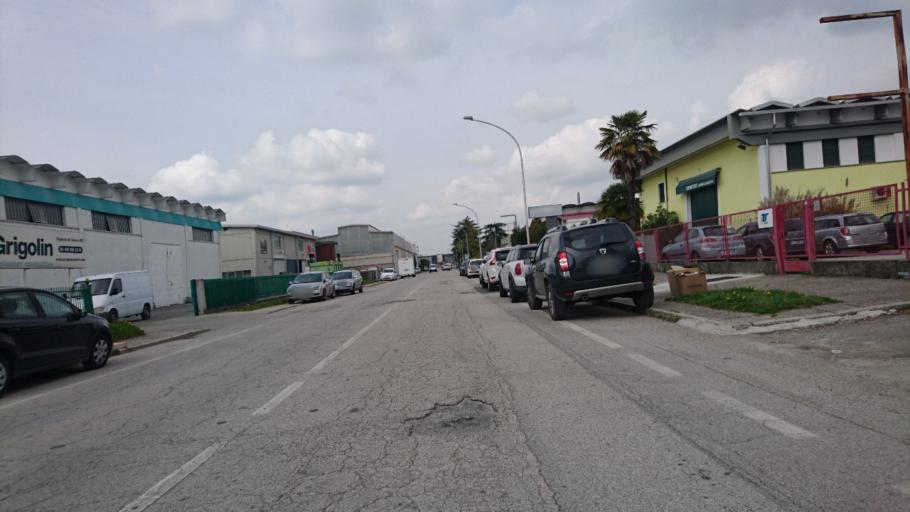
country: IT
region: Veneto
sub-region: Provincia di Padova
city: Saletto
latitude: 45.4626
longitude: 11.8574
